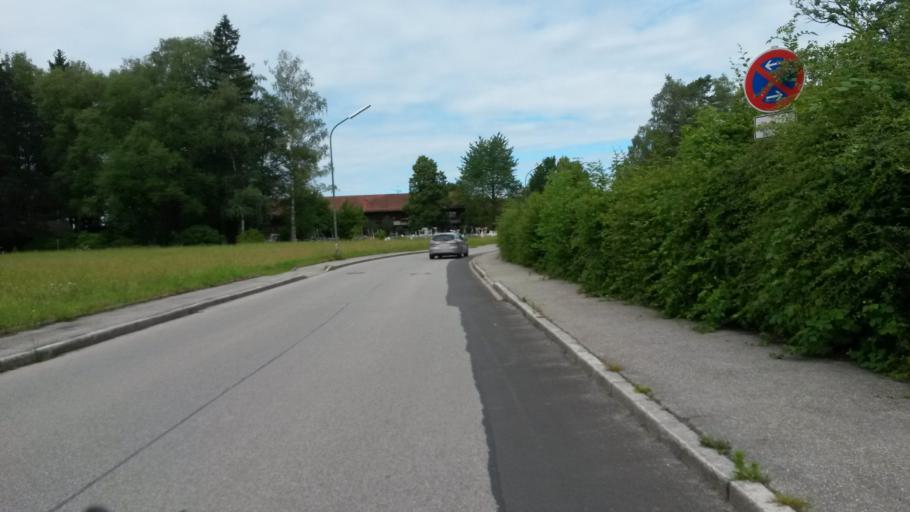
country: DE
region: Bavaria
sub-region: Upper Bavaria
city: Prien am Chiemsee
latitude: 47.8471
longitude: 12.3685
